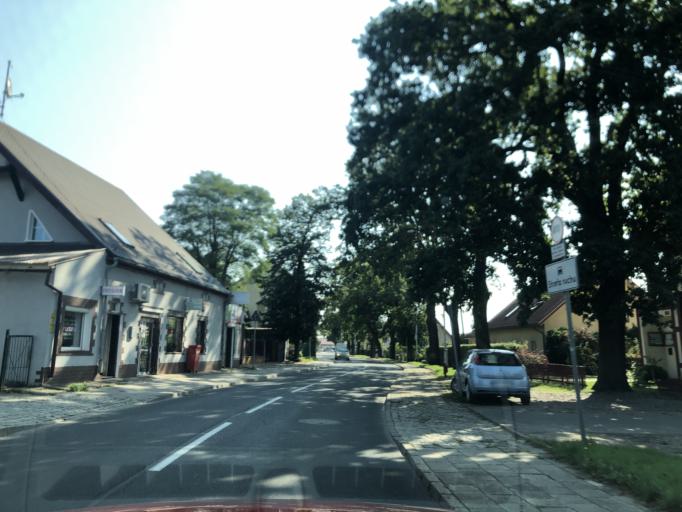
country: PL
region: Lower Silesian Voivodeship
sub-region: Powiat wroclawski
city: Smolec
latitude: 51.1742
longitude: 16.9097
